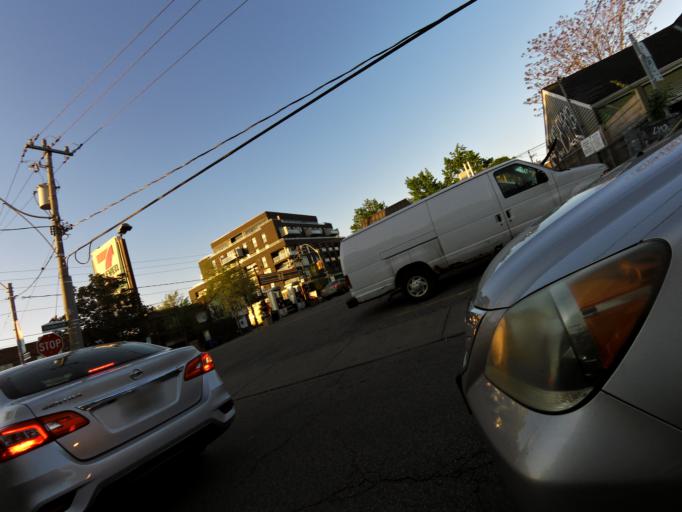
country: CA
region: Ontario
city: Toronto
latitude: 43.6509
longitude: -79.4115
